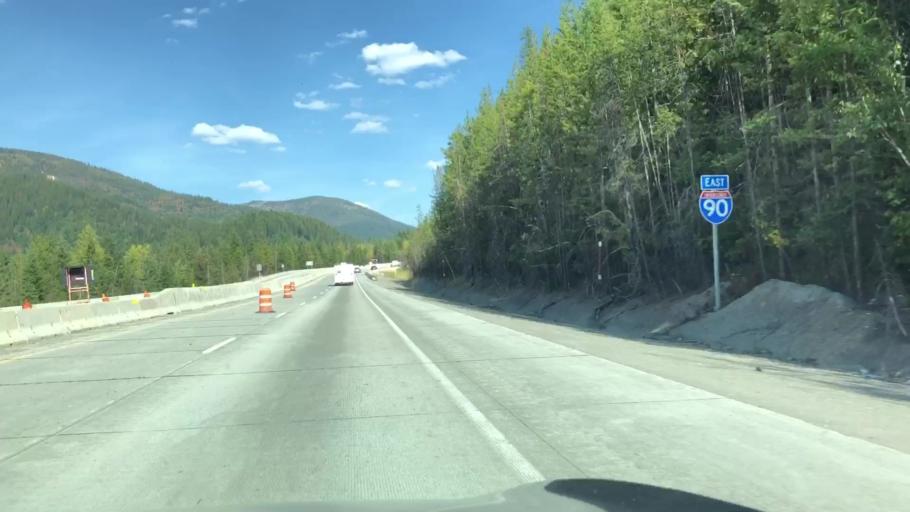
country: US
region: Idaho
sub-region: Shoshone County
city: Wallace
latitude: 47.4693
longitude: -115.7693
